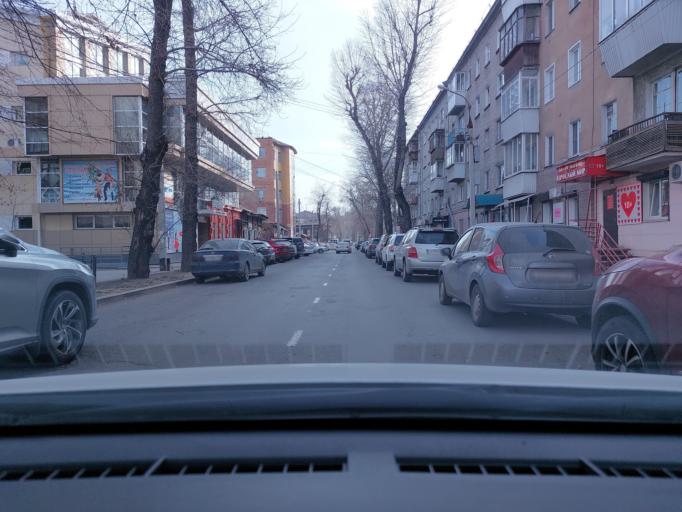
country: RU
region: Irkutsk
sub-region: Irkutskiy Rayon
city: Irkutsk
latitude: 52.2812
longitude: 104.2880
